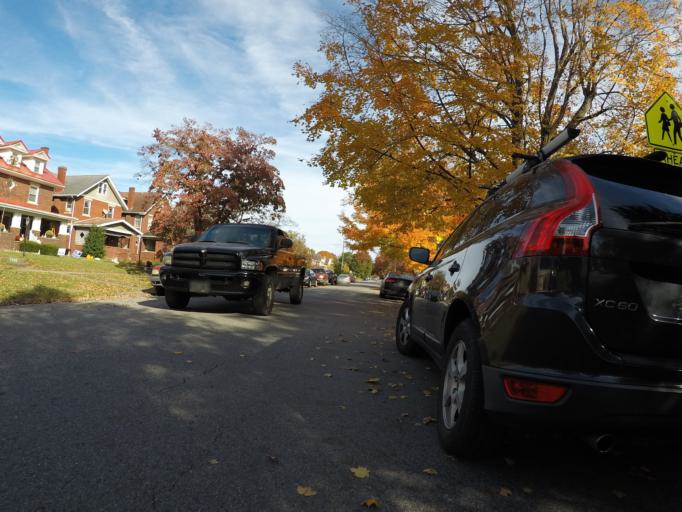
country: US
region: West Virginia
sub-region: Cabell County
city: Huntington
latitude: 38.4114
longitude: -82.4550
